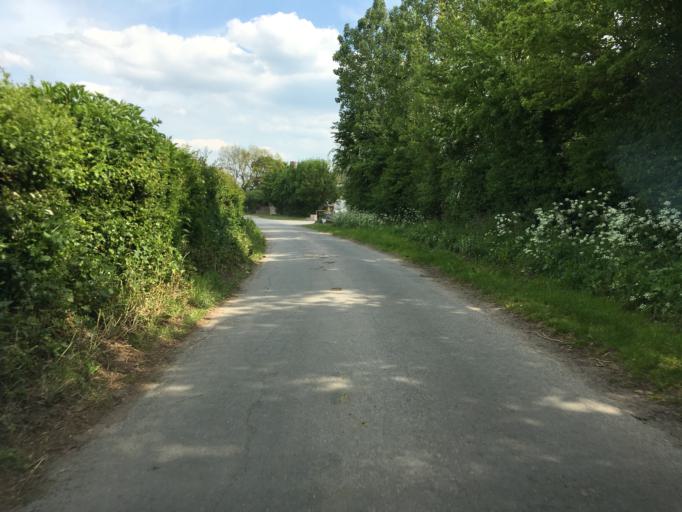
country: GB
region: England
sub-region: South Gloucestershire
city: Thornbury
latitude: 51.6236
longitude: -2.5513
